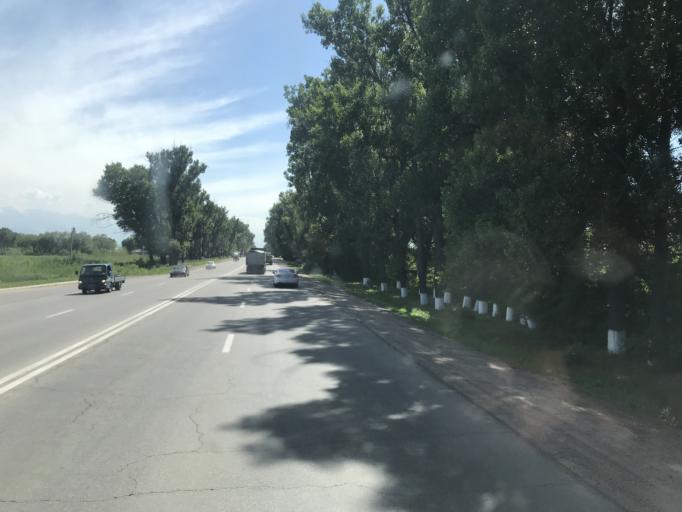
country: KZ
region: Almaty Oblysy
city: Energeticheskiy
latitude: 43.3597
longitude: 77.0764
